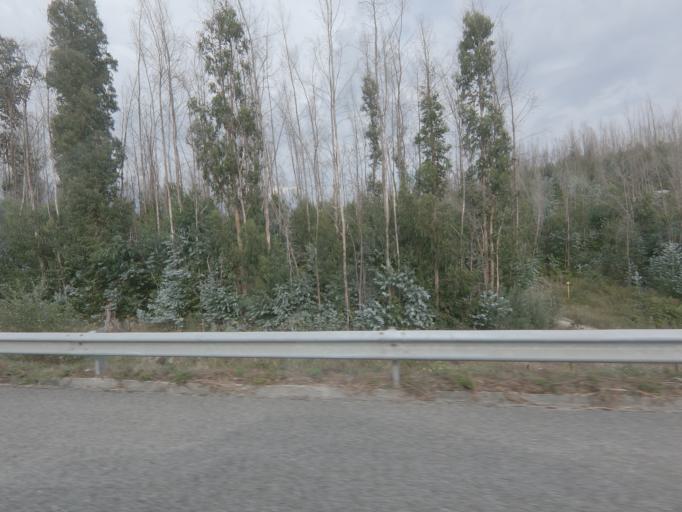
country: PT
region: Viseu
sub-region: Santa Comba Dao
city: Santa Comba Dao
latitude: 40.4499
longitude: -8.1059
